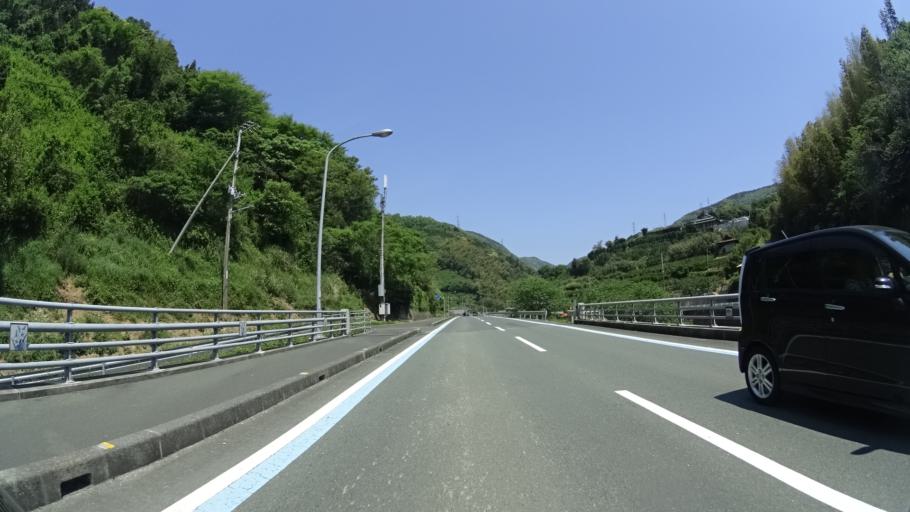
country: JP
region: Ehime
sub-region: Nishiuwa-gun
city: Ikata-cho
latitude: 33.5008
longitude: 132.3964
